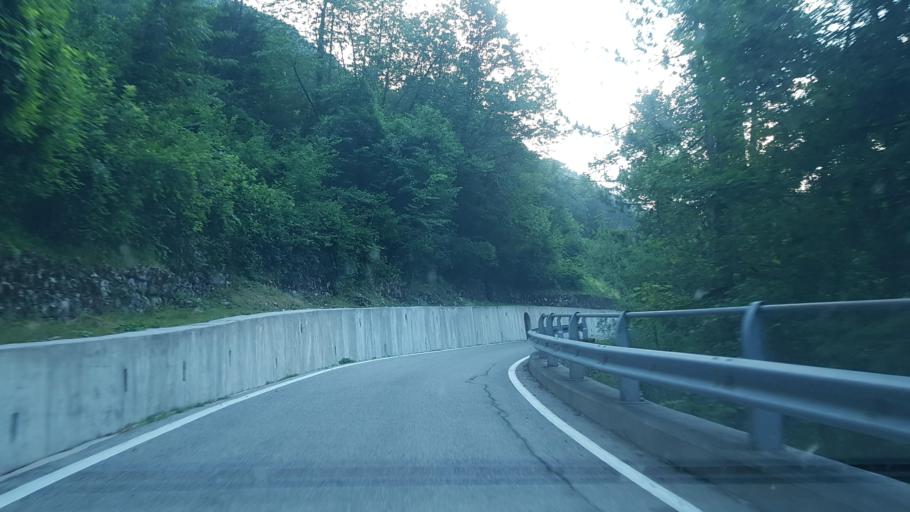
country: IT
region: Friuli Venezia Giulia
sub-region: Provincia di Udine
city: Dogna
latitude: 46.4494
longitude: 13.3333
